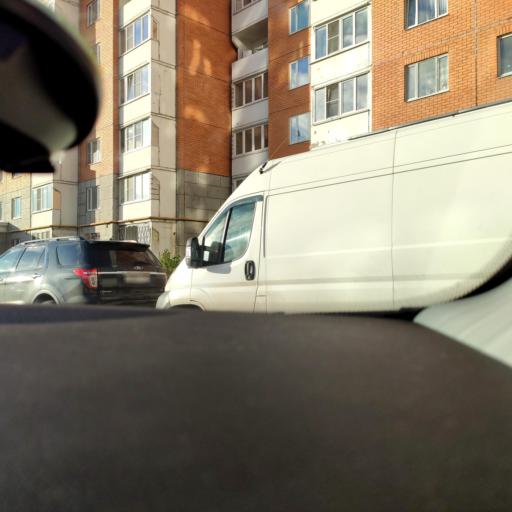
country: RU
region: Moskovskaya
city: Shcherbinka
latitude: 55.4739
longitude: 37.6085
